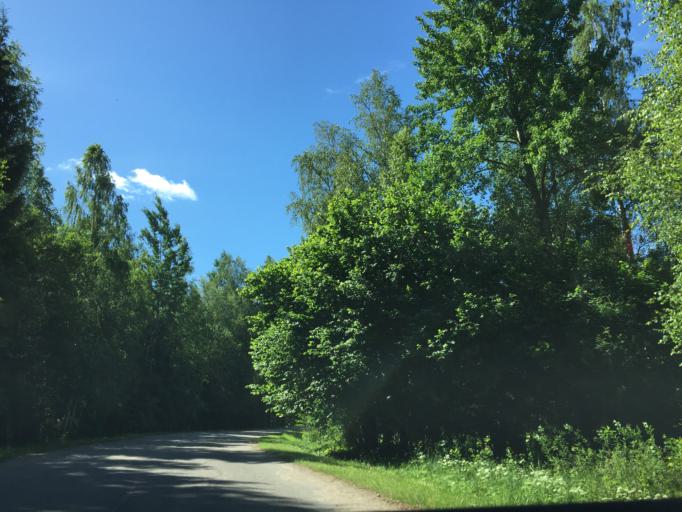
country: LV
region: Dundaga
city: Dundaga
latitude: 57.3552
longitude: 22.0658
